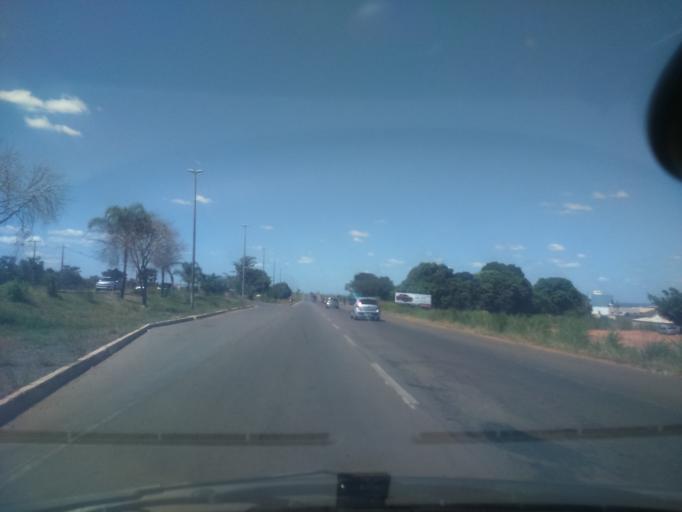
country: BR
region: Goias
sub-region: Luziania
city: Luziania
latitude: -16.0492
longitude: -47.9860
